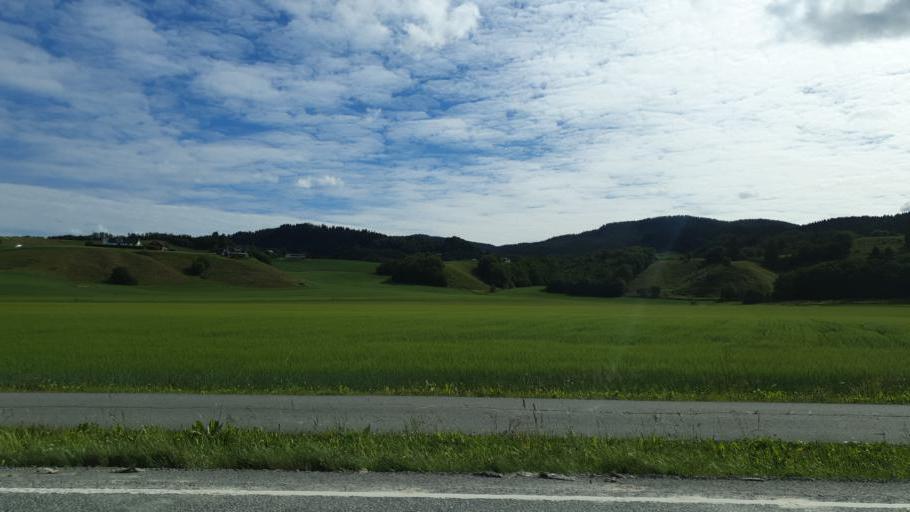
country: NO
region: Sor-Trondelag
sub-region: Melhus
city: Lundamo
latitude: 63.1797
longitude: 10.3165
